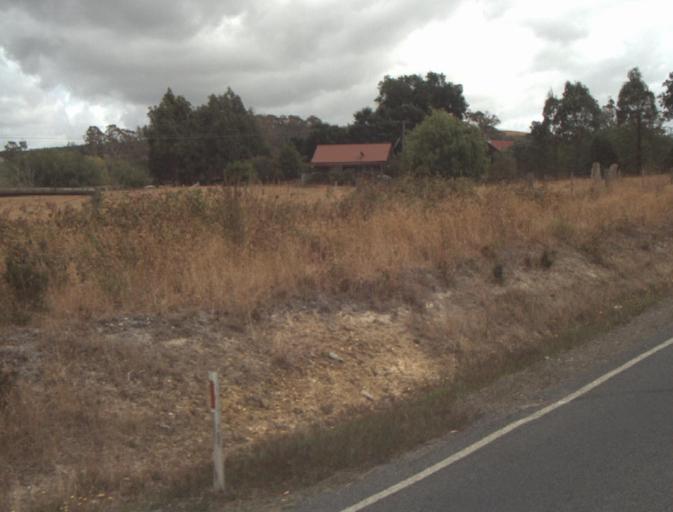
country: AU
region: Tasmania
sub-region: Launceston
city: Mayfield
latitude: -41.2316
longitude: 147.2100
